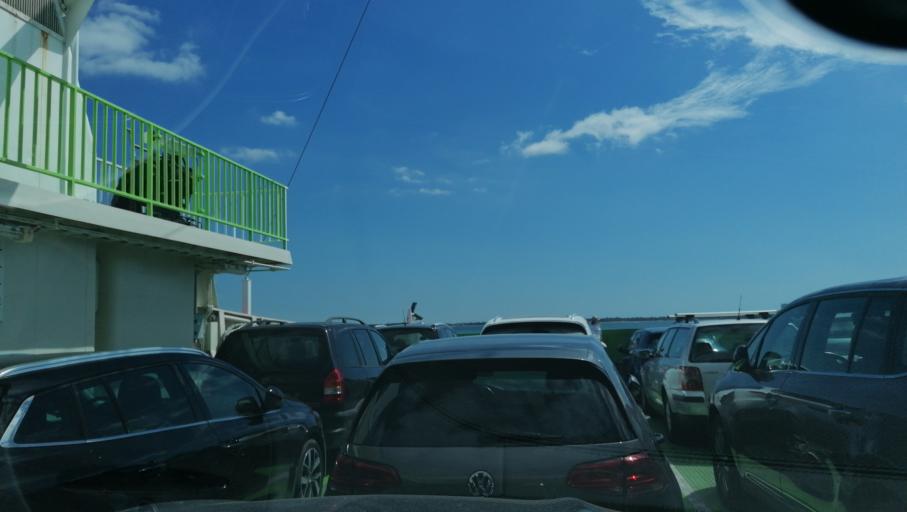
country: PT
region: Setubal
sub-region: Setubal
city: Setubal
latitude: 38.5147
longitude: -8.8856
